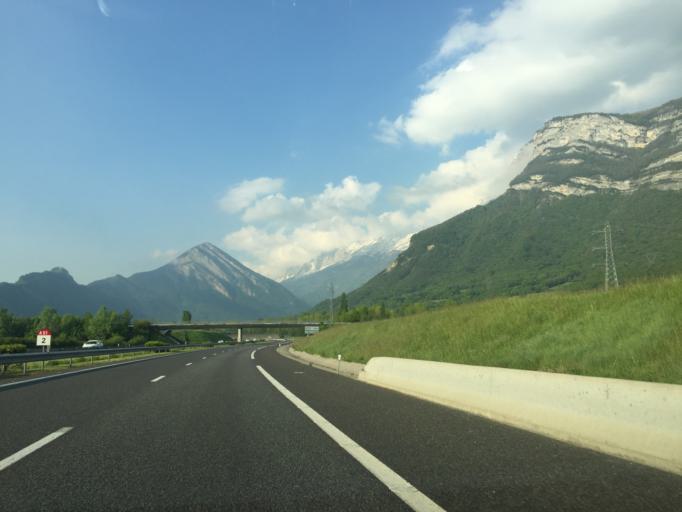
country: FR
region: Rhone-Alpes
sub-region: Departement de l'Isere
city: Allieres-et-Risset
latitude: 45.0990
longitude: 5.6742
